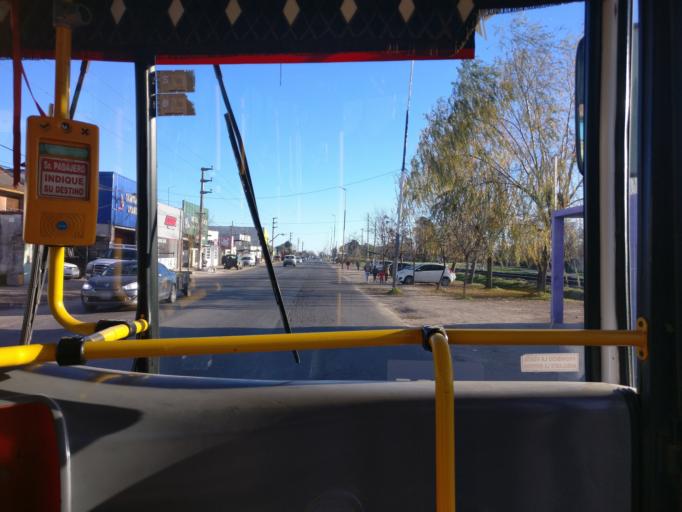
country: AR
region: Buenos Aires
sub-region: Partido de Ezeiza
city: Ezeiza
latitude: -34.8935
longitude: -58.5729
